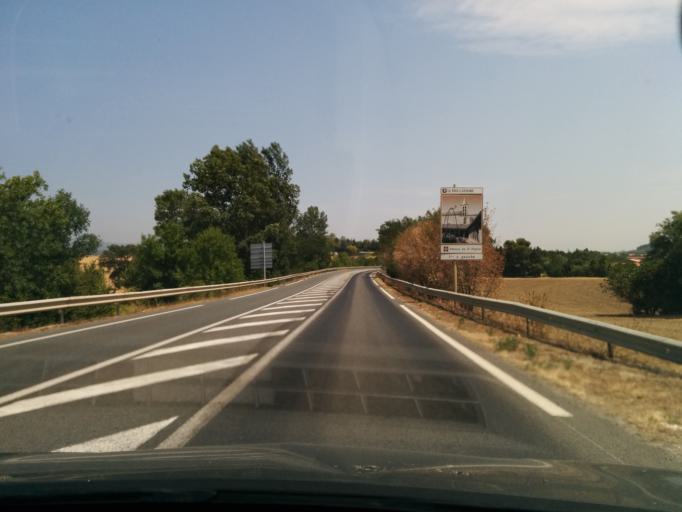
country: FR
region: Languedoc-Roussillon
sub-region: Departement de l'Aude
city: Castelnaudary
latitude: 43.3248
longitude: 1.9554
